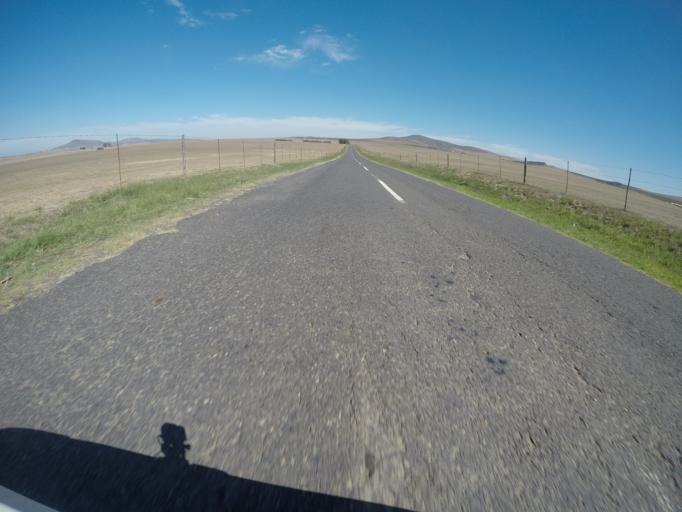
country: ZA
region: Western Cape
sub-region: City of Cape Town
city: Atlantis
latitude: -33.6872
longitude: 18.5977
